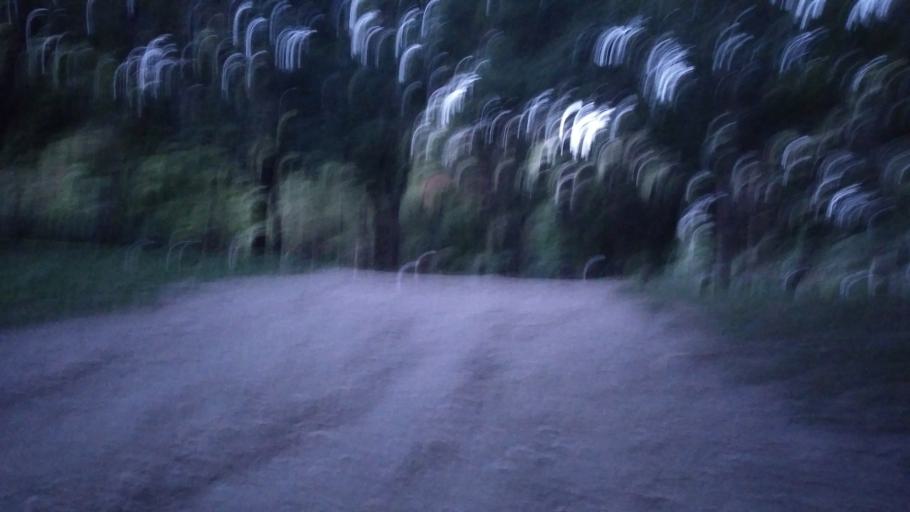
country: HU
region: Budapest
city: Budapest III. keruelet
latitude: 47.5587
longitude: 19.0604
